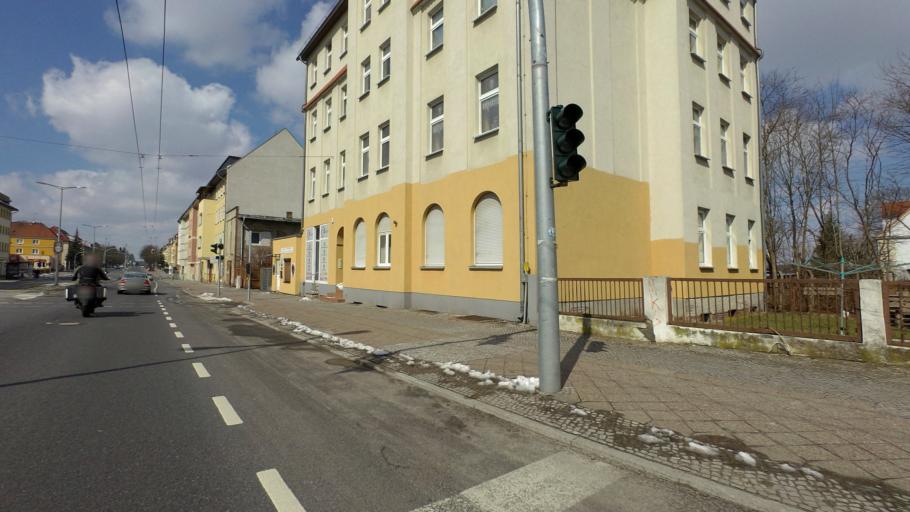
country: DE
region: Brandenburg
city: Eberswalde
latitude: 52.8362
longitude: 13.7894
